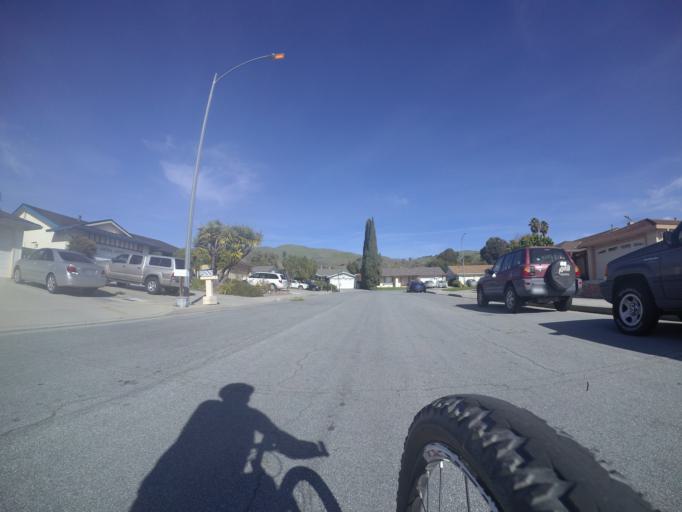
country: US
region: California
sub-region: Santa Clara County
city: Milpitas
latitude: 37.4134
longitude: -121.8596
